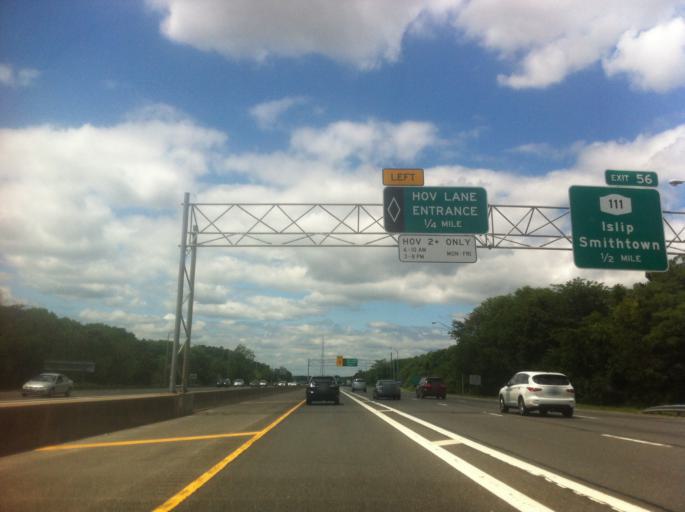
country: US
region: New York
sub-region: Suffolk County
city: Hauppauge
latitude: 40.8093
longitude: -73.2024
